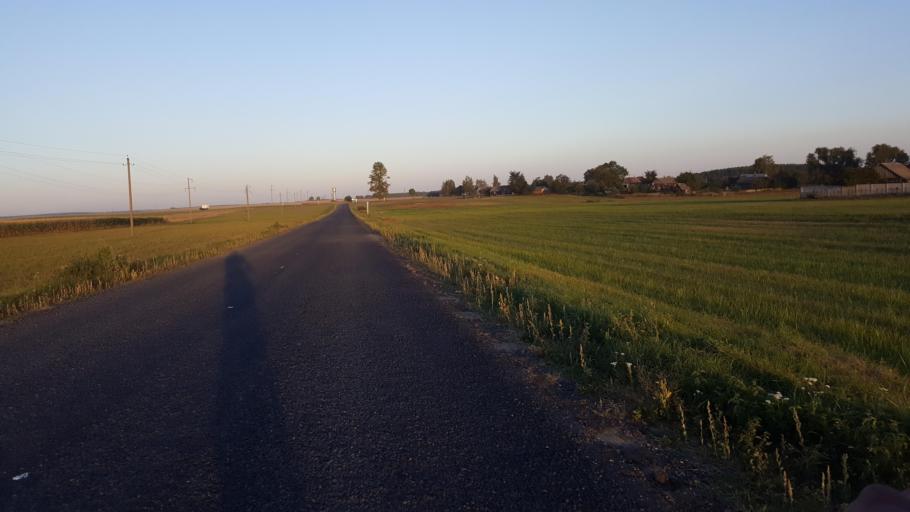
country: BY
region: Brest
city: Charnawchytsy
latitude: 52.2896
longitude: 23.5757
